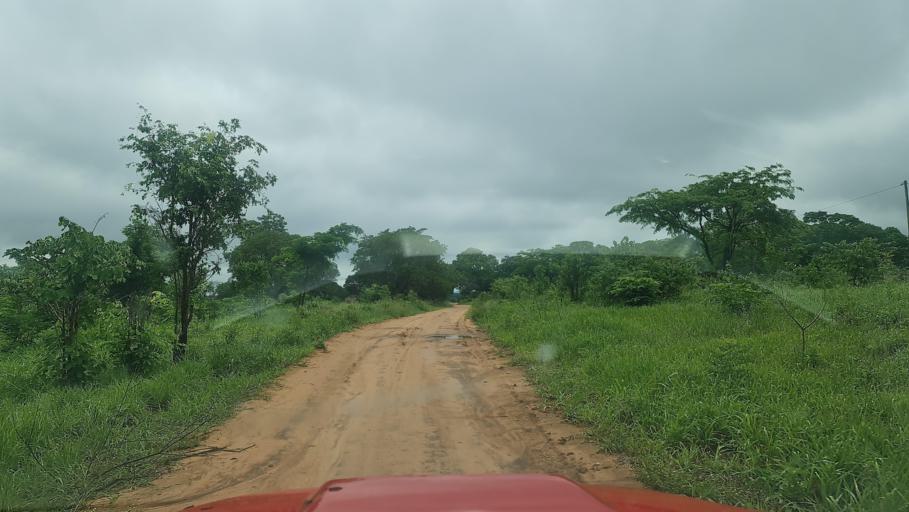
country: MW
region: Southern Region
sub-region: Nsanje District
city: Nsanje
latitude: -17.1929
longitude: 35.8558
